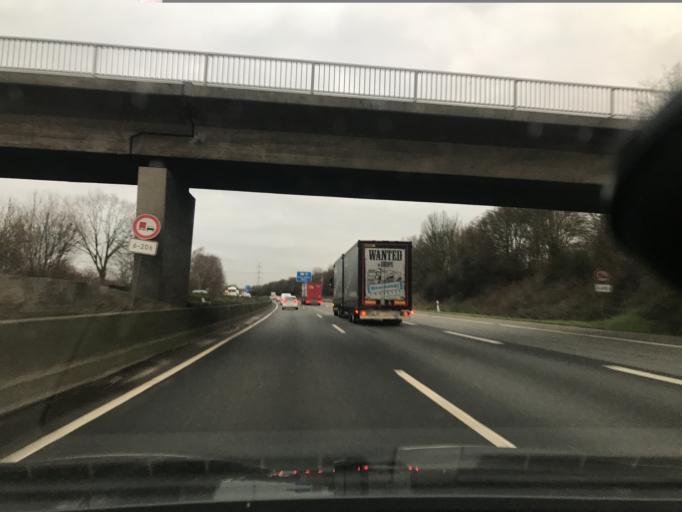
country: DE
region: North Rhine-Westphalia
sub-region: Regierungsbezirk Dusseldorf
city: Moers
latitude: 51.4557
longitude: 6.5919
